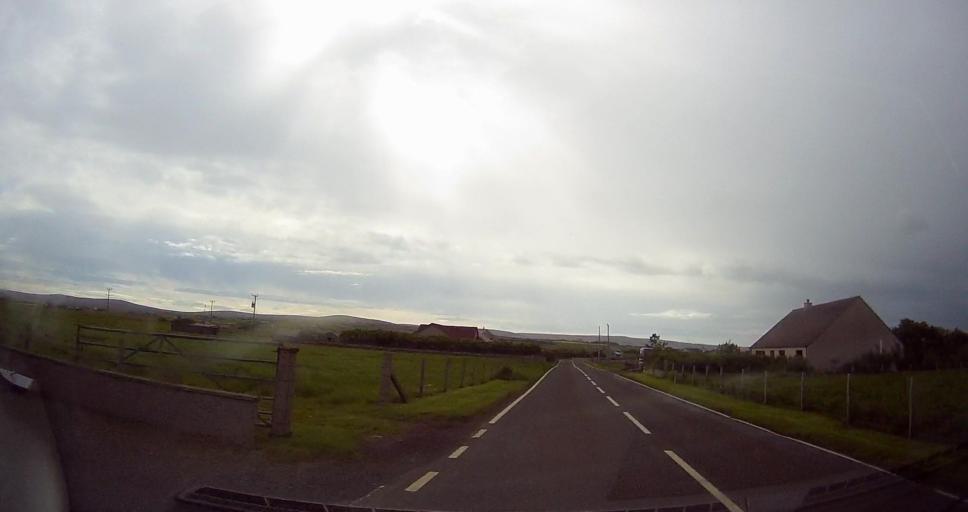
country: GB
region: Scotland
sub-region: Orkney Islands
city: Stromness
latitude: 59.0733
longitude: -3.2415
